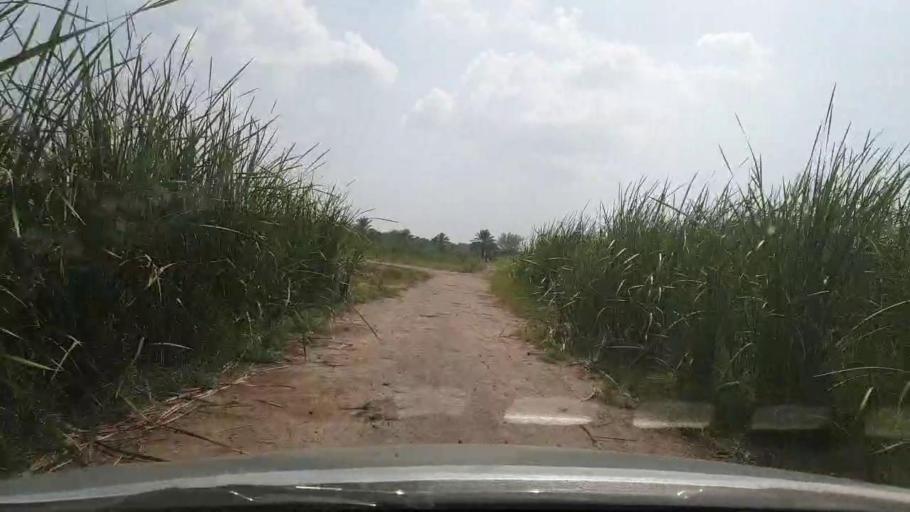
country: PK
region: Sindh
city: Khairpur
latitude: 27.4618
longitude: 68.7771
